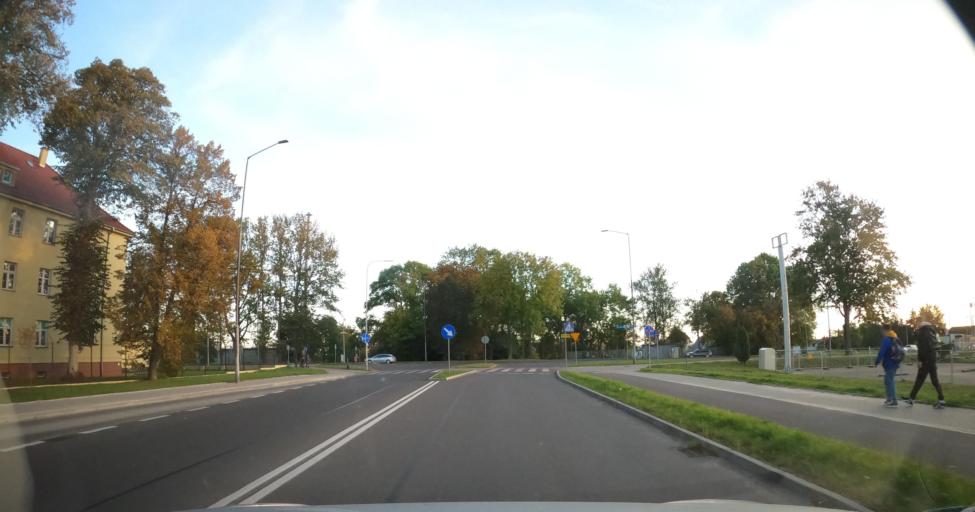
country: PL
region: West Pomeranian Voivodeship
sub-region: Powiat kolobrzeski
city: Kolobrzeg
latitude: 54.1765
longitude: 15.6011
